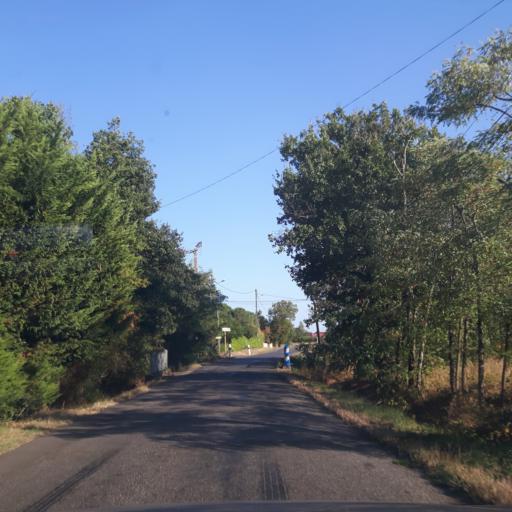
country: FR
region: Midi-Pyrenees
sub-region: Departement de la Haute-Garonne
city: Villaudric
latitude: 43.8049
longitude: 1.4397
